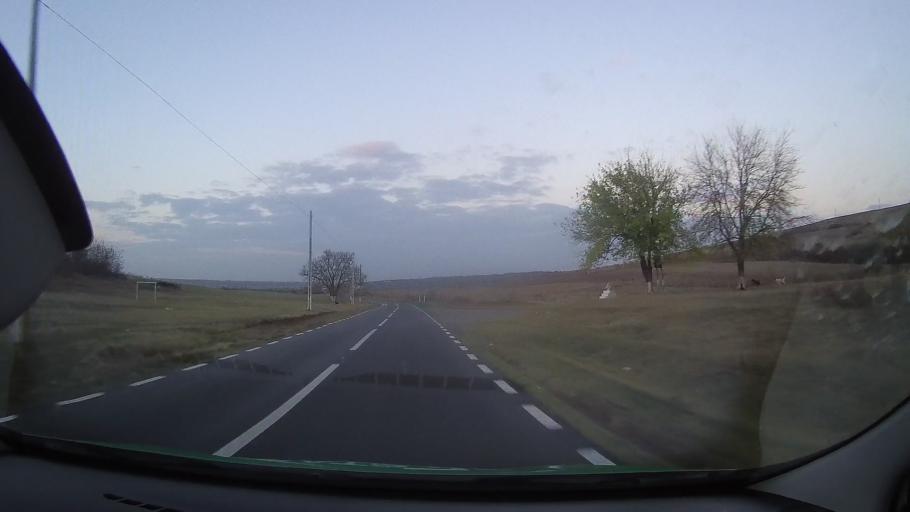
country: RO
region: Constanta
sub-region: Comuna Oltina
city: Oltina
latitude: 44.1504
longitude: 27.6675
